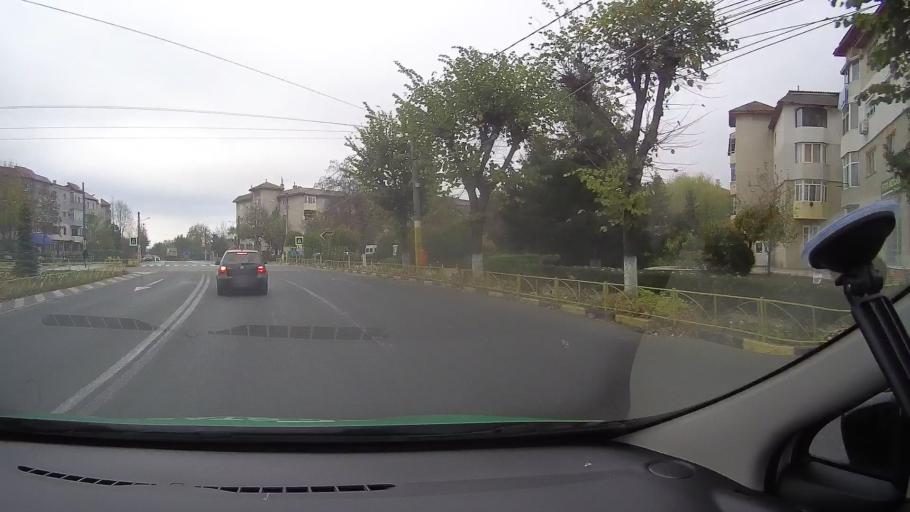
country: RO
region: Constanta
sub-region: Oras Murfatlar
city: Murfatlar
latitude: 44.1743
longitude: 28.4111
